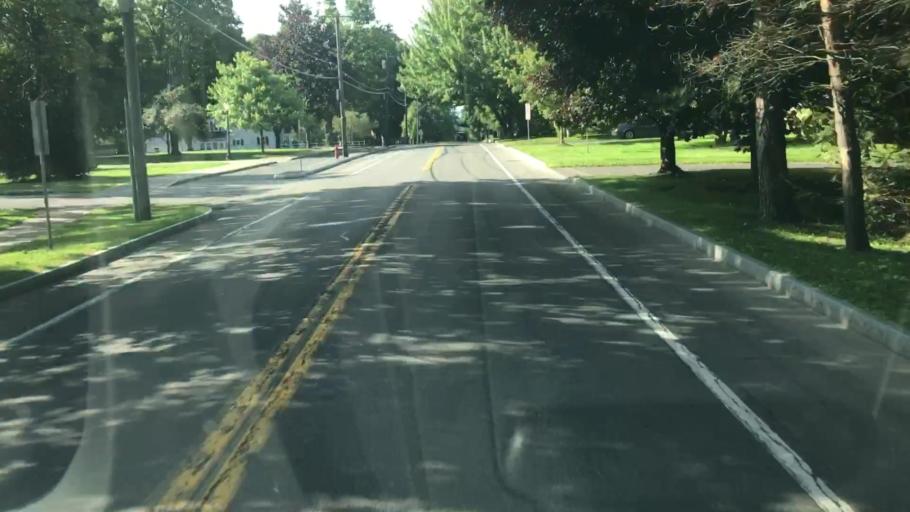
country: US
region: New York
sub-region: Onondaga County
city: Skaneateles
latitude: 42.9524
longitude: -76.4260
